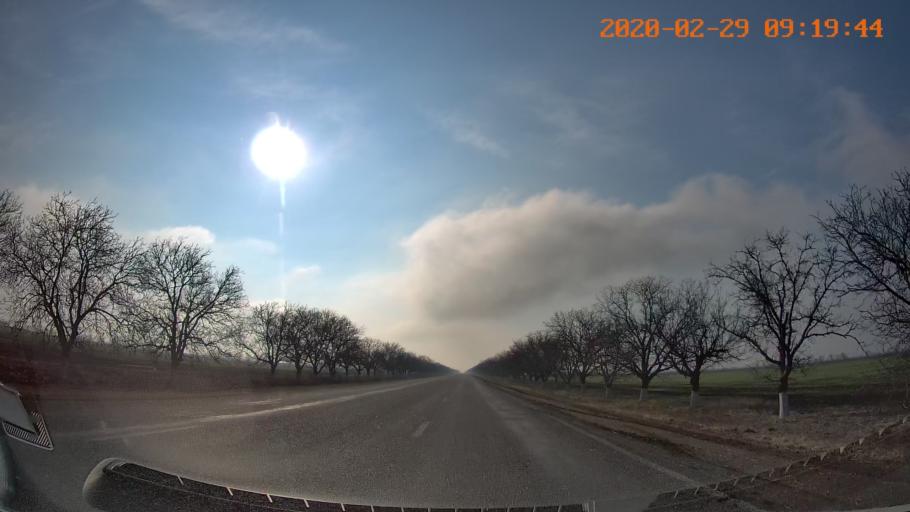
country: MD
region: Telenesti
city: Pervomaisc
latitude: 46.7587
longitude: 29.9419
